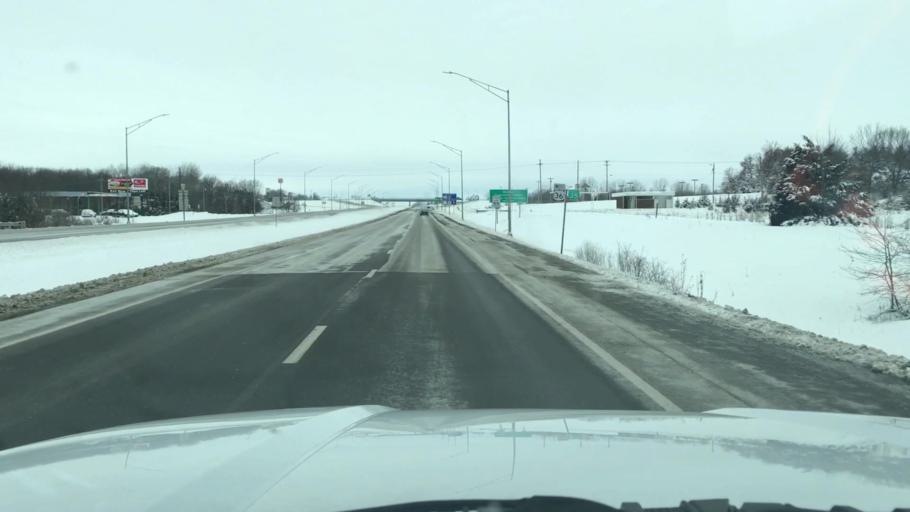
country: US
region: Missouri
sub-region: Clinton County
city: Cameron
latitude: 39.7540
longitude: -94.2221
